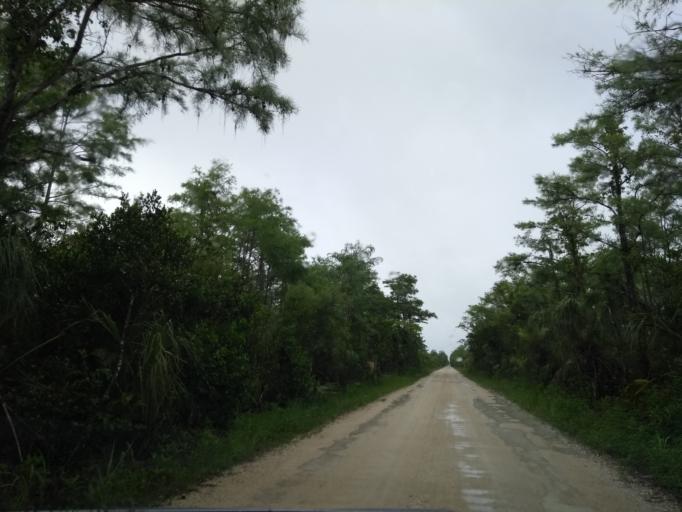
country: US
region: Florida
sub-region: Miami-Dade County
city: The Hammocks
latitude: 25.7602
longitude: -81.0321
